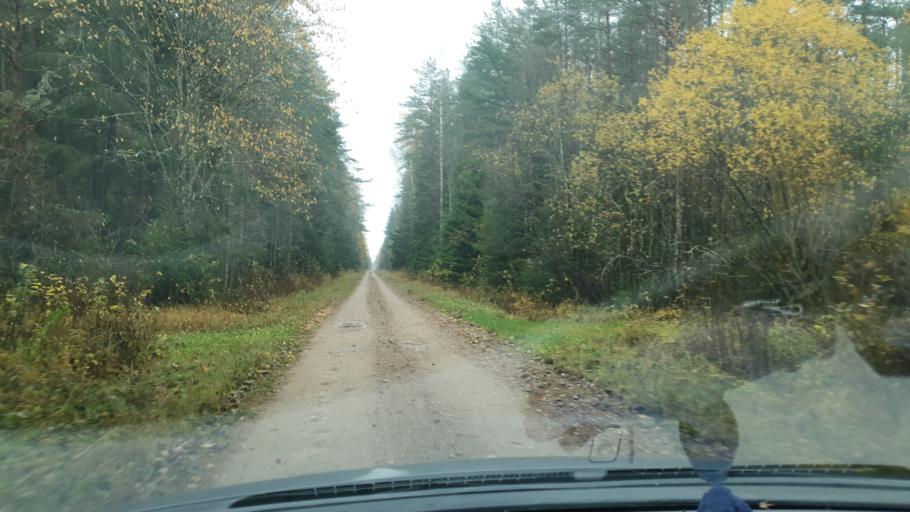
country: EE
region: Viljandimaa
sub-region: Karksi vald
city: Karksi-Nuia
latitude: 57.9767
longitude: 25.6215
